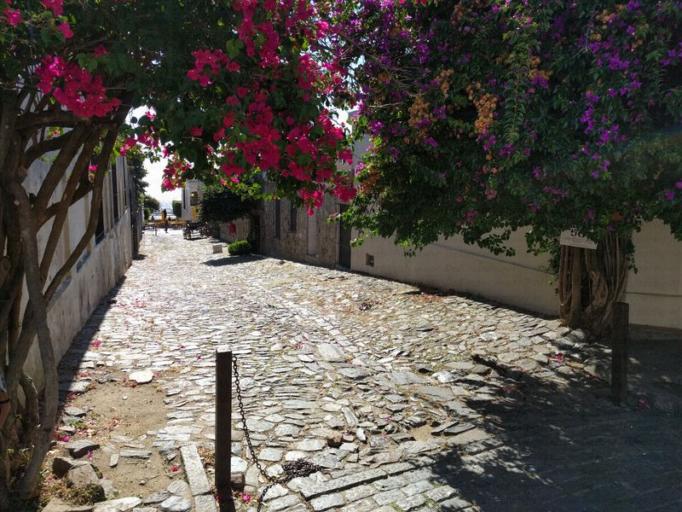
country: UY
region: Colonia
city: Colonia del Sacramento
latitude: -34.4716
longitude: -57.8519
